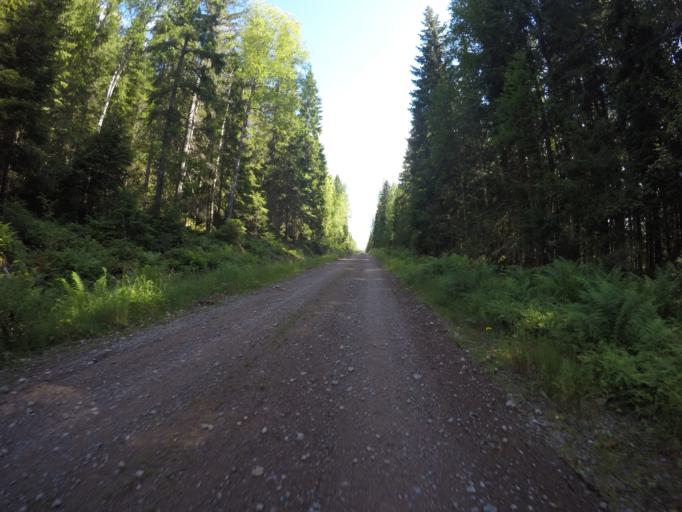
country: SE
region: OErebro
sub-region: Hallefors Kommun
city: Haellefors
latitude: 59.9907
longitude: 14.6075
